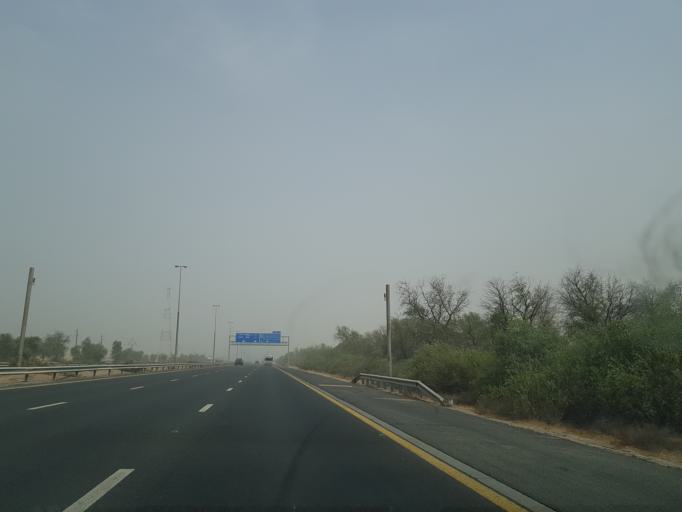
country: AE
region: Dubai
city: Dubai
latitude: 24.9392
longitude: 55.5121
